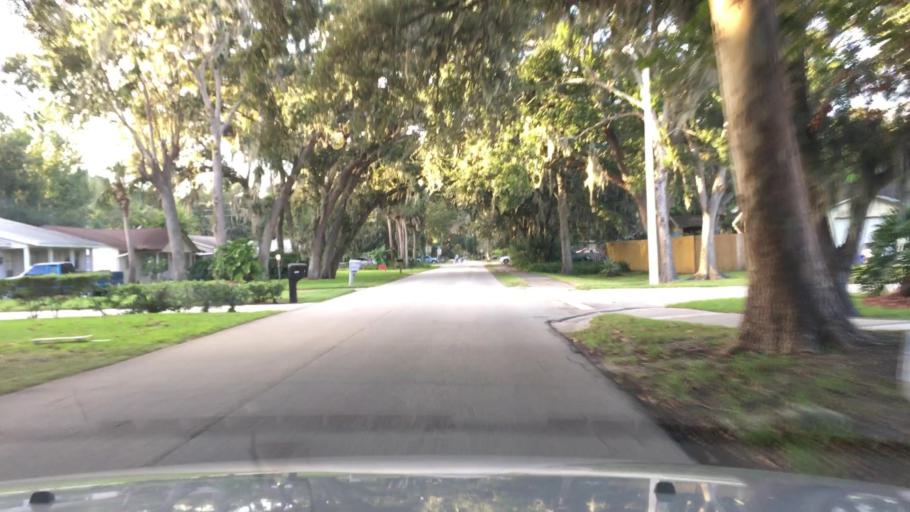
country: US
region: Florida
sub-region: Volusia County
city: Ormond Beach
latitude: 29.2672
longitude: -81.0638
